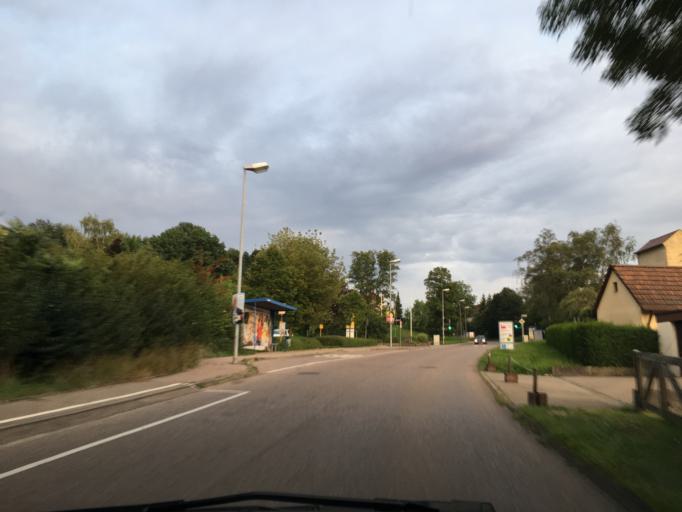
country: DE
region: Baden-Wuerttemberg
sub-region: Regierungsbezirk Stuttgart
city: Esslingen
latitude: 48.7224
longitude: 9.3169
